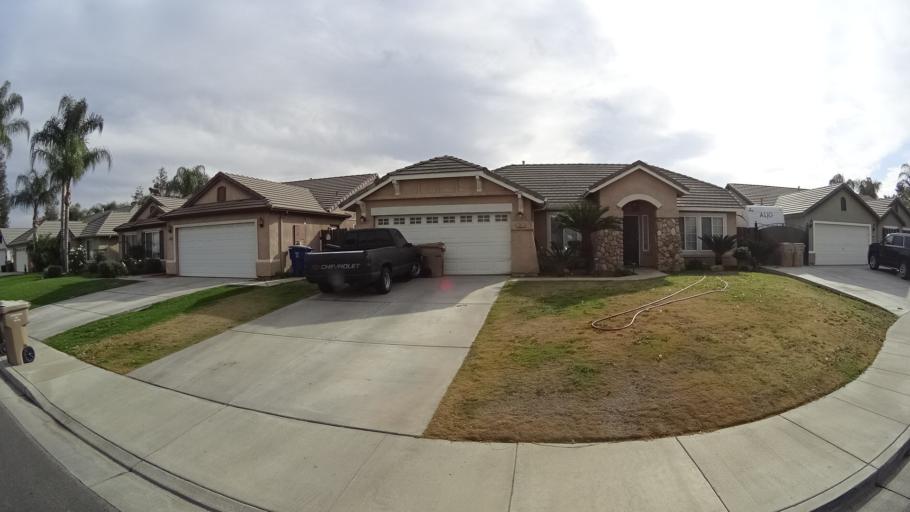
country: US
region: California
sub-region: Kern County
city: Rosedale
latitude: 35.4182
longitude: -119.1446
